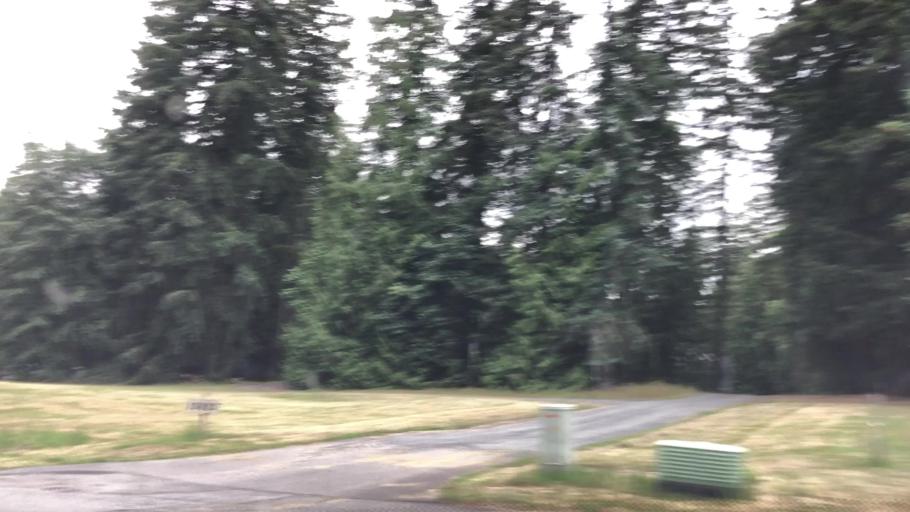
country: US
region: Washington
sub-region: King County
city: Cottage Lake
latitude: 47.7226
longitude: -122.0940
